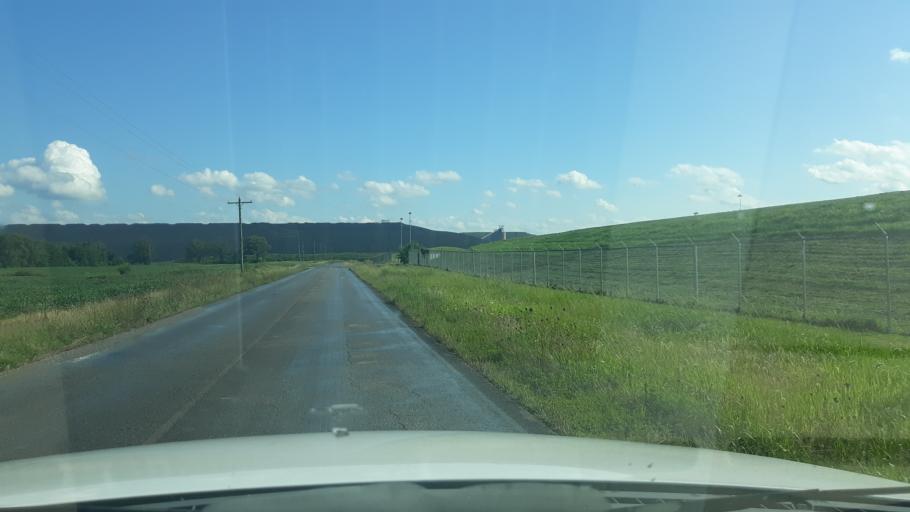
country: US
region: Illinois
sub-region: Saline County
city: Harrisburg
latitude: 37.8394
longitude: -88.5814
